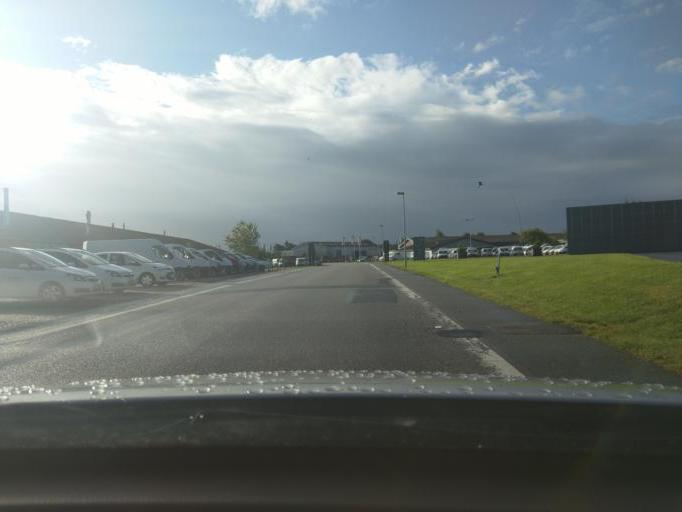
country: DK
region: Central Jutland
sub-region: Viborg Kommune
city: Viborg
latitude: 56.4686
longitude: 9.3971
